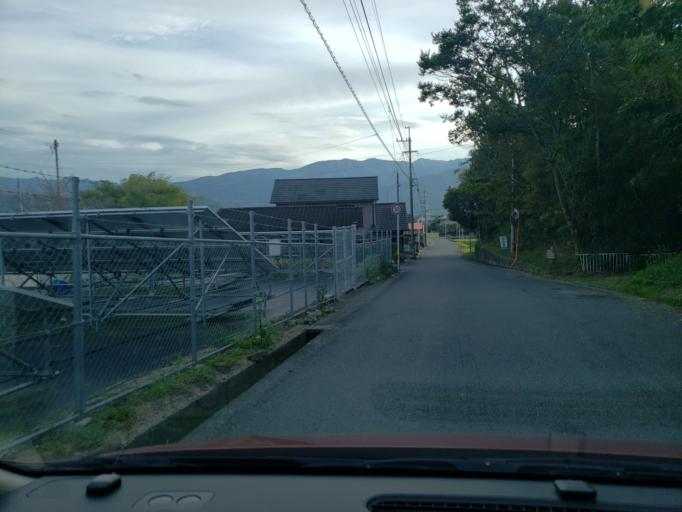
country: JP
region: Tokushima
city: Wakimachi
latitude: 34.0773
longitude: 134.2280
